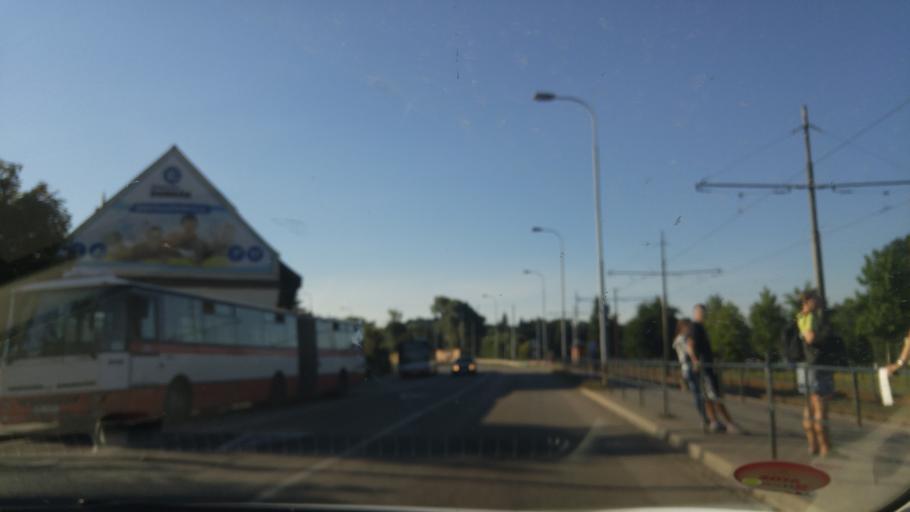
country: CZ
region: South Moravian
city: Troubsko
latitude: 49.2278
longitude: 16.5317
